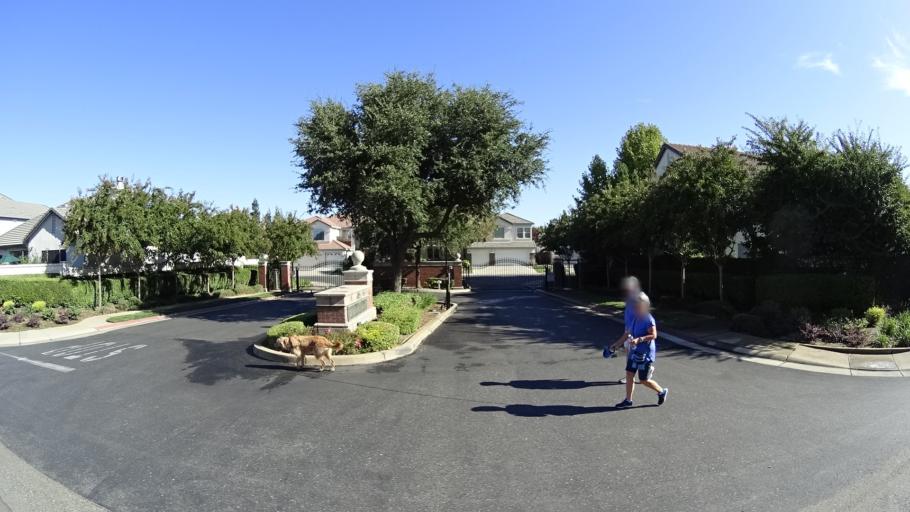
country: US
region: California
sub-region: Sacramento County
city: Laguna
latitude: 38.4105
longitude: -121.4755
